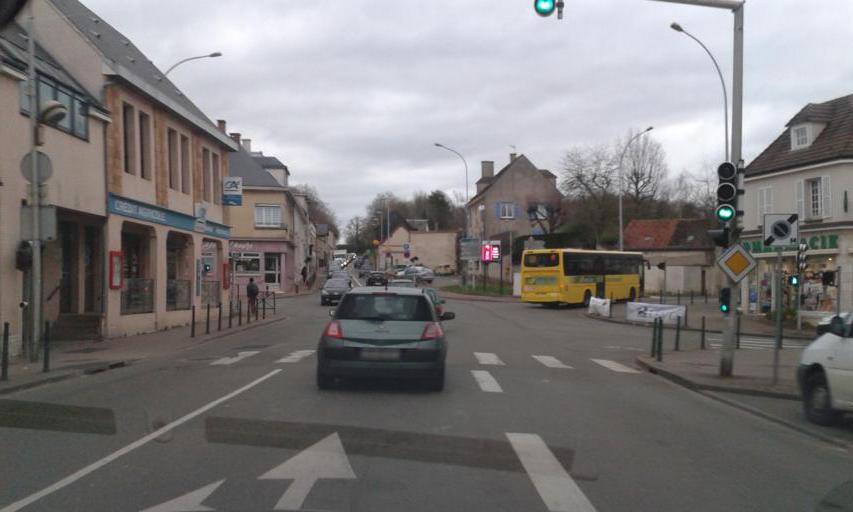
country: FR
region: Centre
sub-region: Departement d'Eure-et-Loir
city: Leves
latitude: 48.4696
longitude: 1.4807
